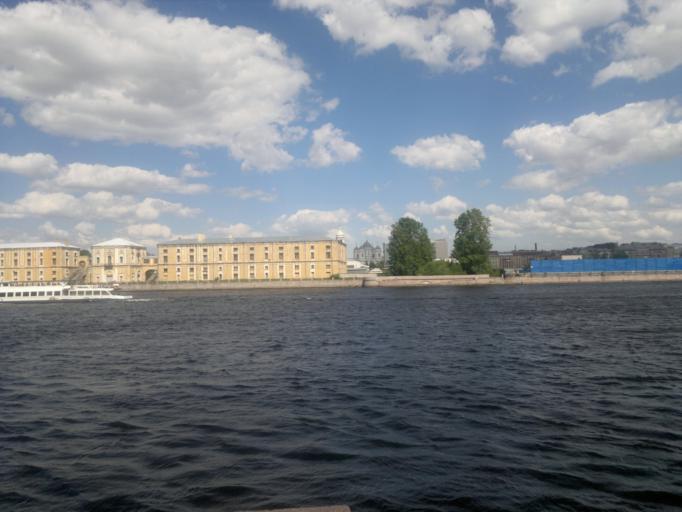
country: RU
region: St.-Petersburg
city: Saint Petersburg
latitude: 59.9462
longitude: 30.2911
